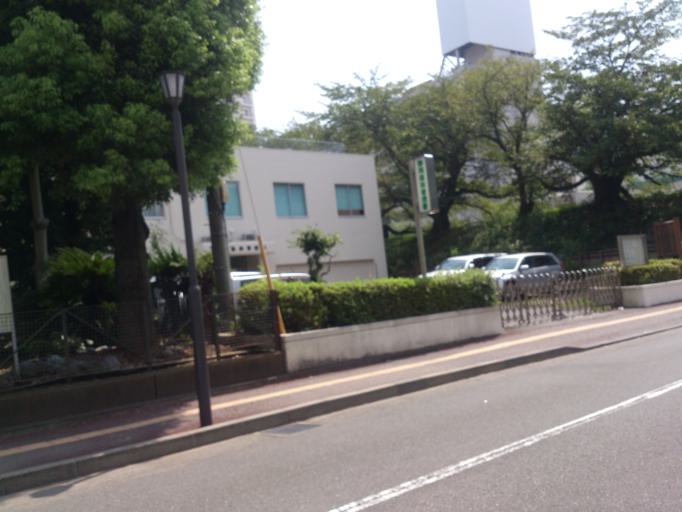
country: JP
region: Shizuoka
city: Shizuoka-shi
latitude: 34.9762
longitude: 138.3850
